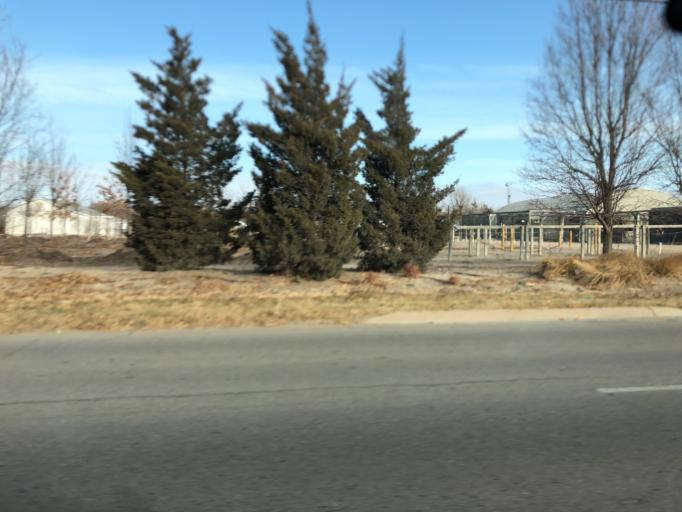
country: US
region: Kansas
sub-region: Reno County
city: Hutchinson
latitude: 38.0572
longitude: -97.9608
